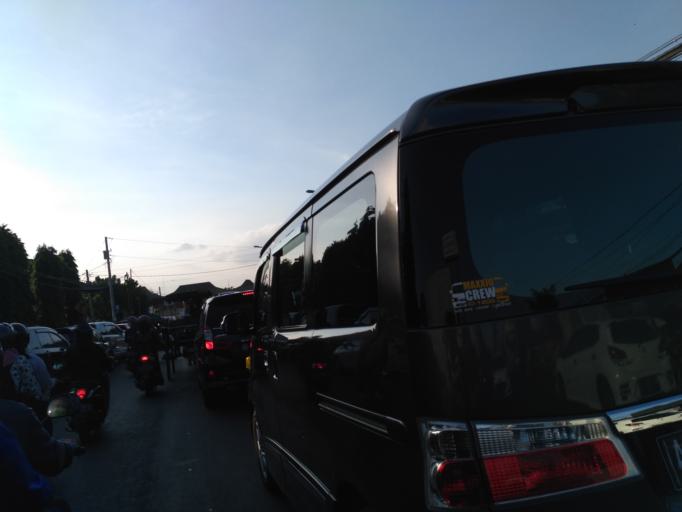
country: ID
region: Daerah Istimewa Yogyakarta
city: Sewon
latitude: -7.8337
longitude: 110.3905
